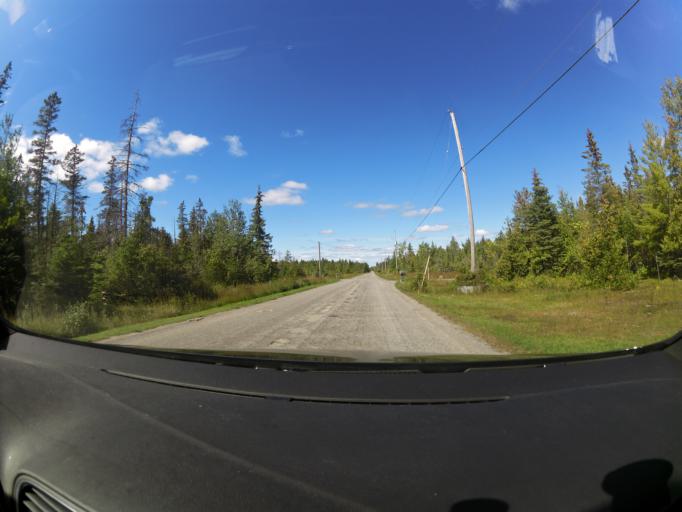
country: CA
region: Ontario
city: Carleton Place
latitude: 45.2503
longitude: -76.1711
